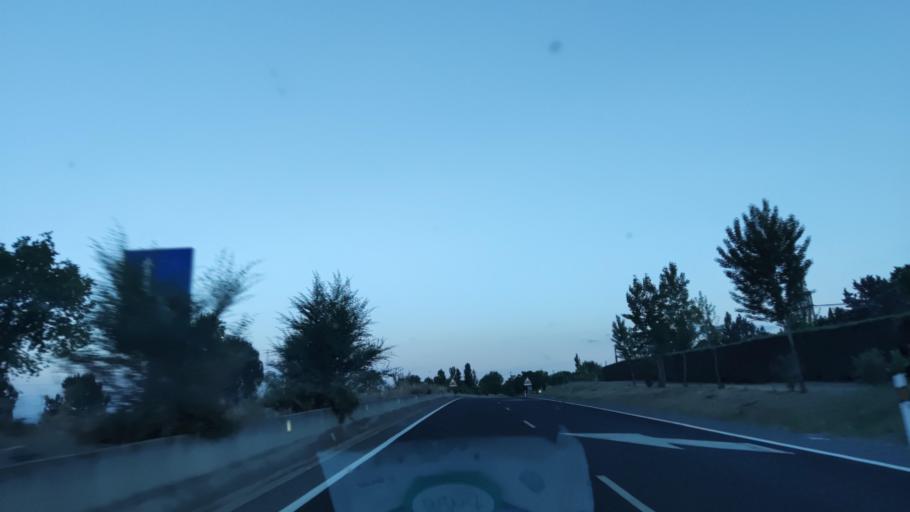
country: ES
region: Madrid
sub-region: Provincia de Madrid
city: San Sebastian de los Reyes
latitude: 40.5180
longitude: -3.5922
